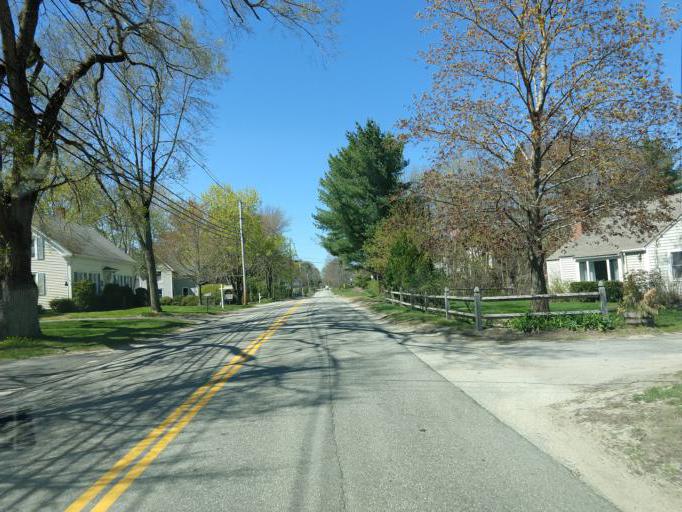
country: US
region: Maine
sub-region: York County
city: Arundel
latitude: 43.3740
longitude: -70.4751
